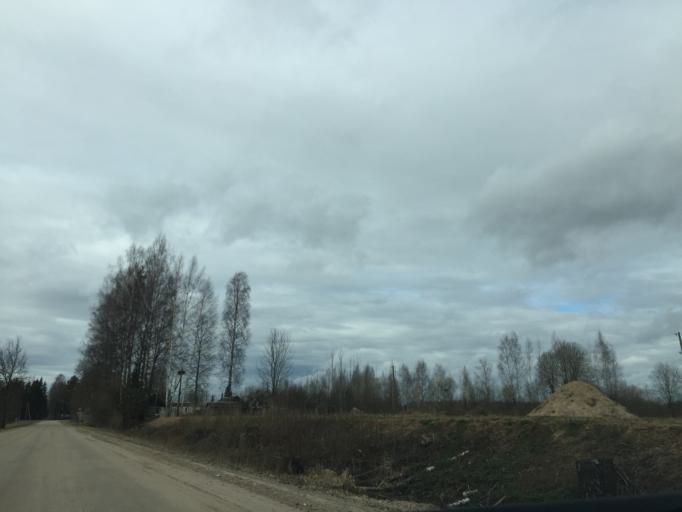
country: LV
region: Daugavpils
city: Daugavpils
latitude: 55.9646
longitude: 26.6750
